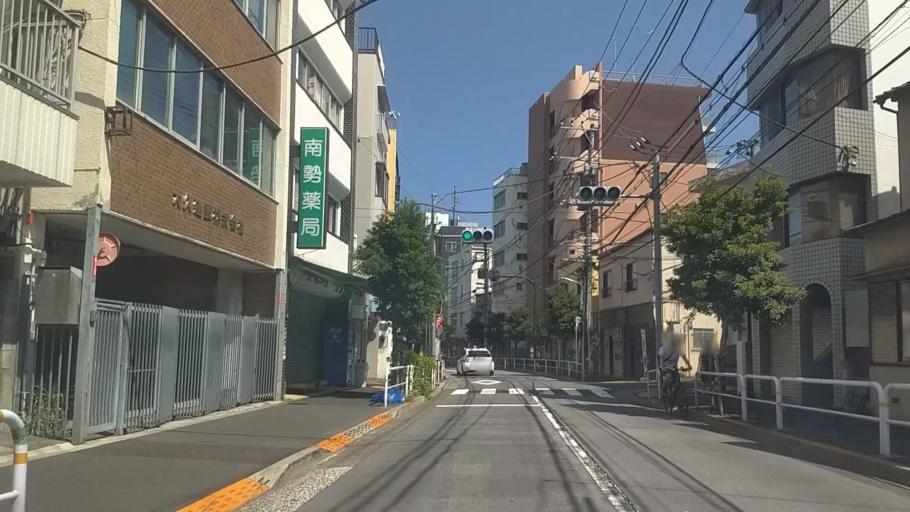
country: JP
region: Tokyo
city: Tokyo
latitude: 35.6167
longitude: 139.7253
